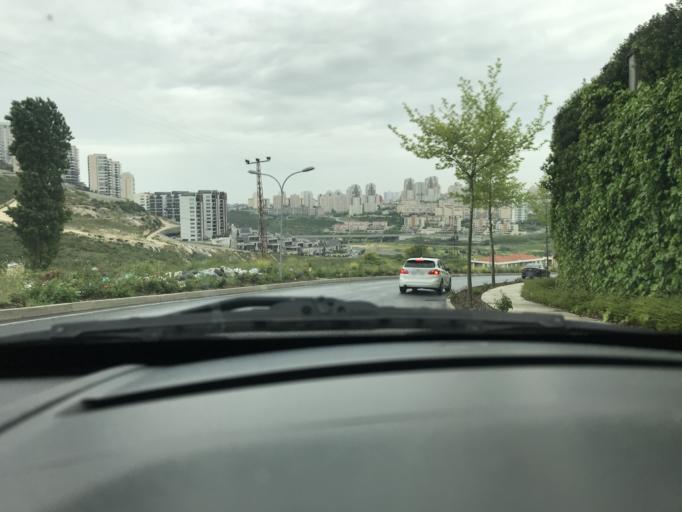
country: TR
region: Istanbul
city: Esenyurt
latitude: 41.0884
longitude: 28.6827
